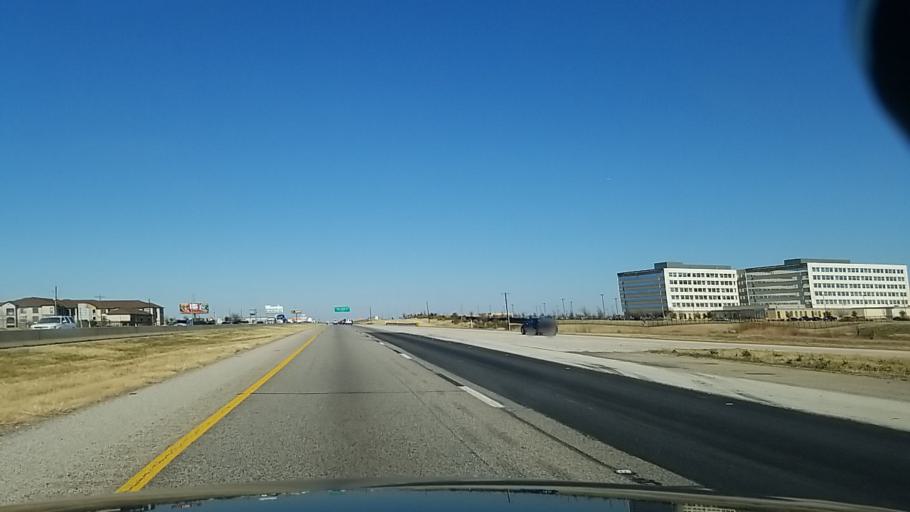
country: US
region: Texas
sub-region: Tarrant County
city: Haslet
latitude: 32.9181
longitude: -97.3170
